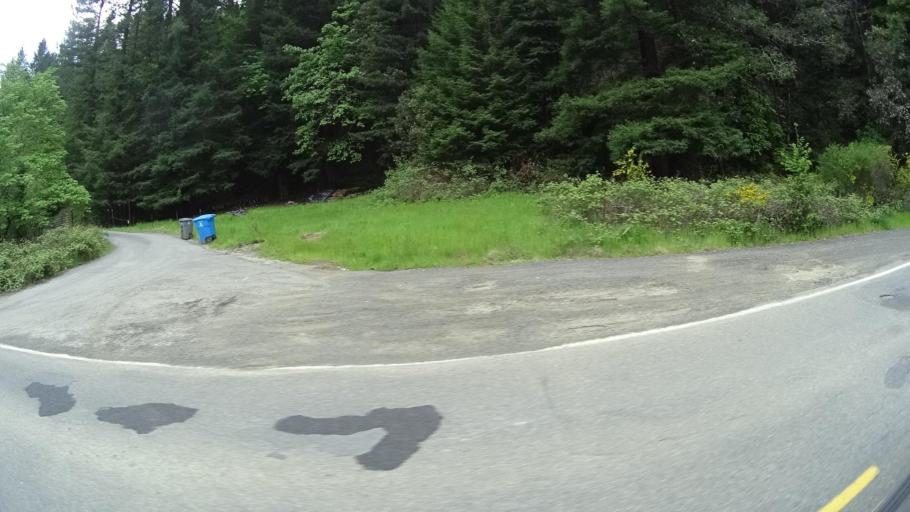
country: US
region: California
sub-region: Humboldt County
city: Redway
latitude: 40.1274
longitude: -123.8528
